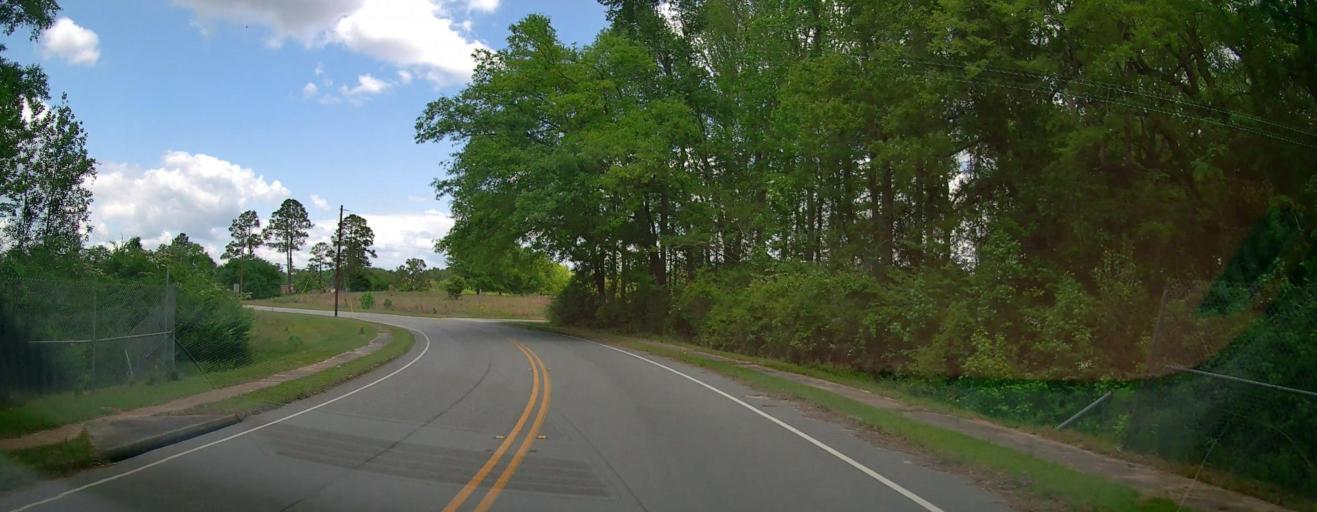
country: US
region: Georgia
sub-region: Treutlen County
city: Soperton
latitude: 32.3767
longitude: -82.5839
